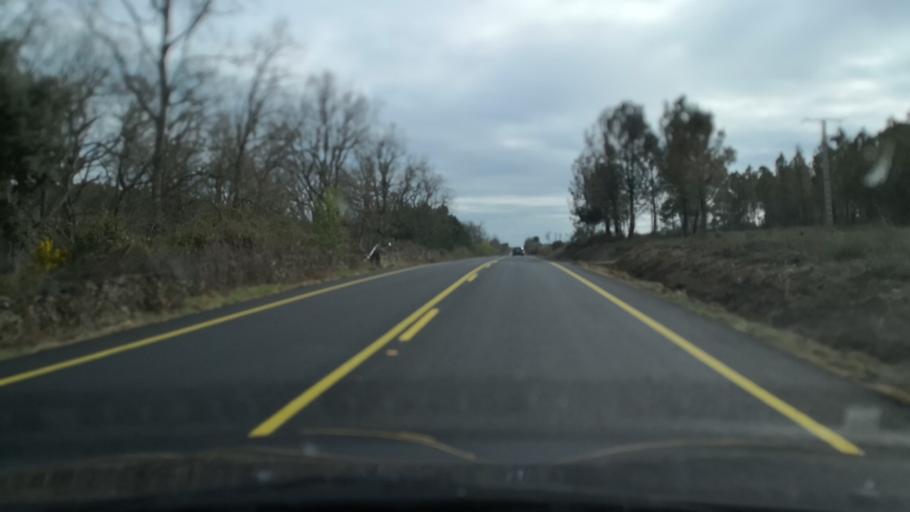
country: ES
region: Castille and Leon
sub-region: Provincia de Salamanca
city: Robleda
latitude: 40.3673
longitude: -6.6199
